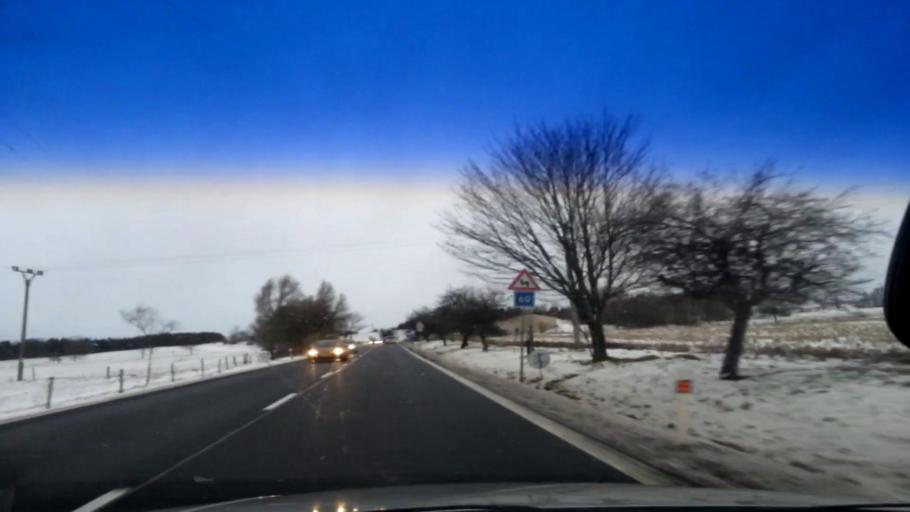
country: CZ
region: Karlovarsky
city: Hazlov
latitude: 50.1696
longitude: 12.2627
